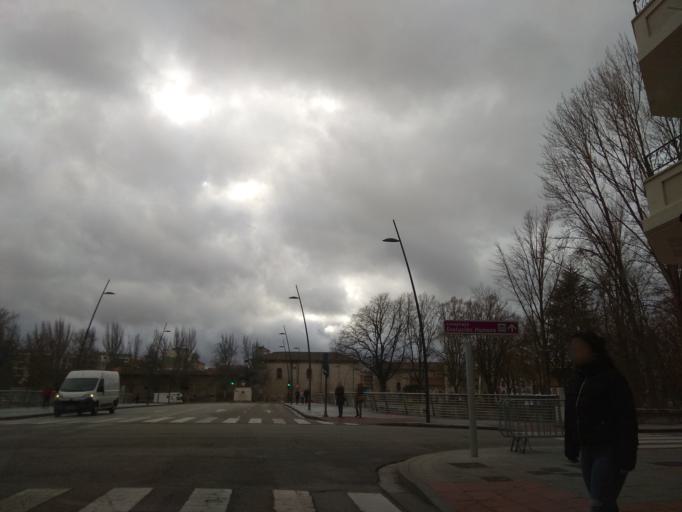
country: ES
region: Castille and Leon
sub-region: Provincia de Burgos
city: Burgos
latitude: 42.3417
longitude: -3.6947
